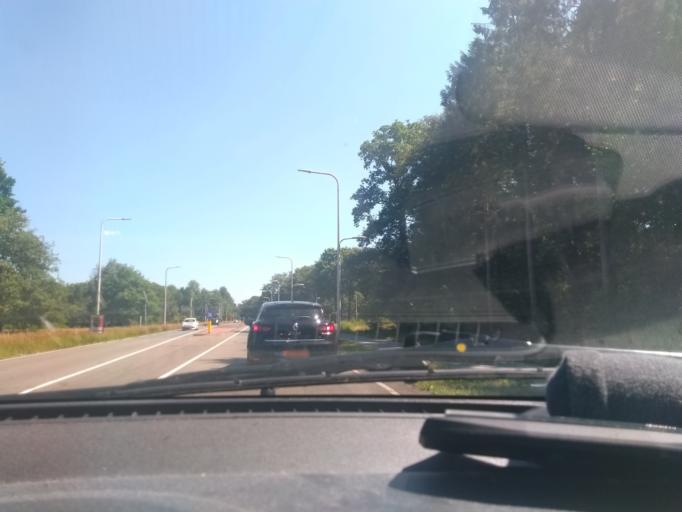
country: NL
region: Drenthe
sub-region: Gemeente Assen
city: Assen
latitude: 52.9931
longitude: 6.5896
